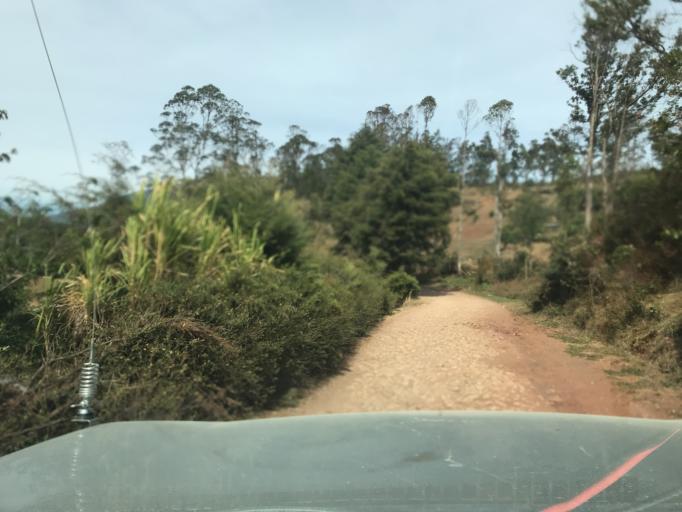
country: TL
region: Ainaro
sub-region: Ainaro
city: Ainaro
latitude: -8.8843
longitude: 125.5360
